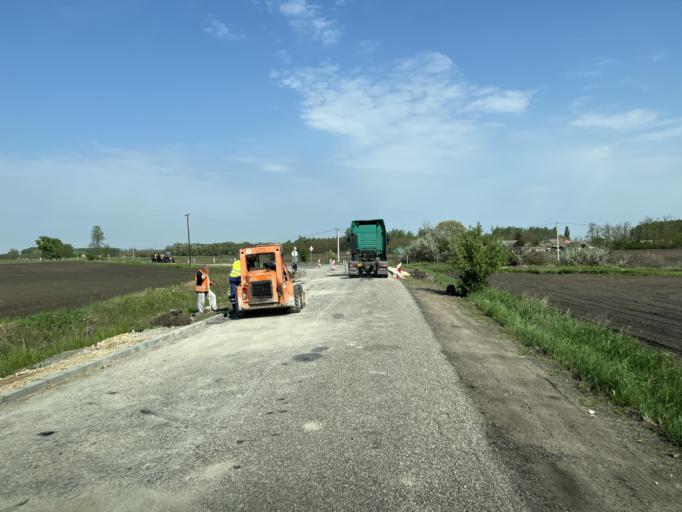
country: HU
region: Pest
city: Kocser
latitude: 46.9858
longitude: 19.9800
